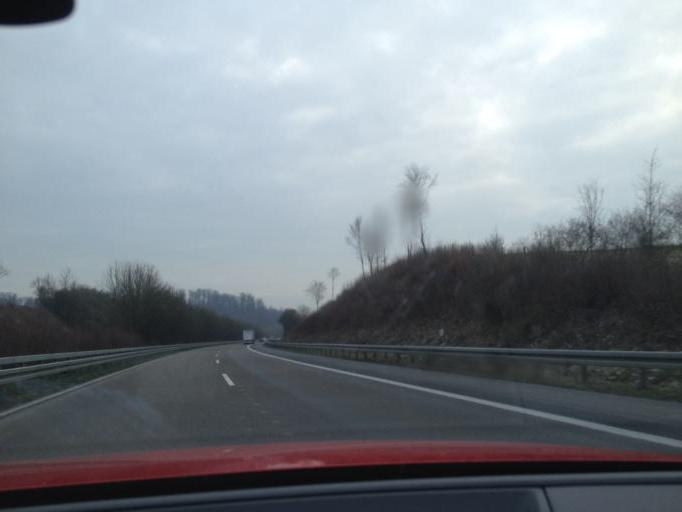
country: DE
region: Hesse
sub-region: Regierungsbezirk Darmstadt
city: Hammersbach
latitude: 50.2291
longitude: 9.0079
